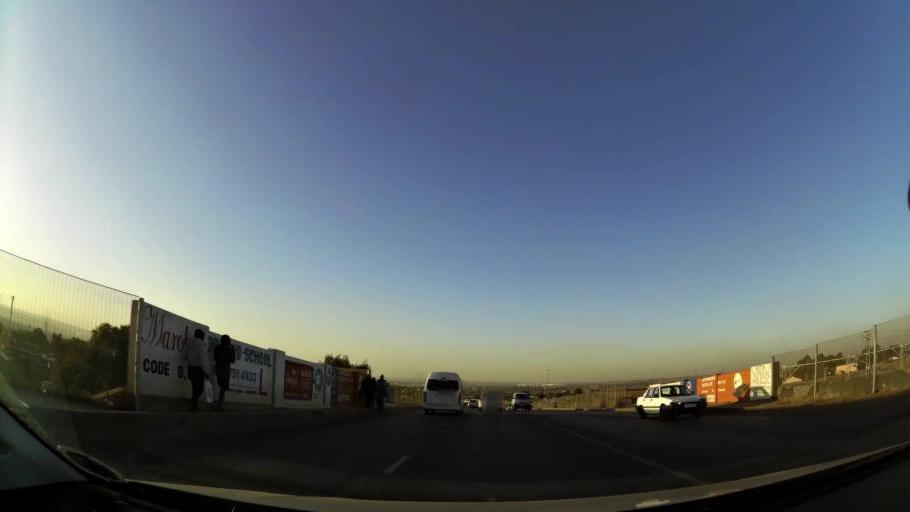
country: ZA
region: Gauteng
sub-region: Ekurhuleni Metropolitan Municipality
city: Tembisa
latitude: -26.0031
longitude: 28.2214
